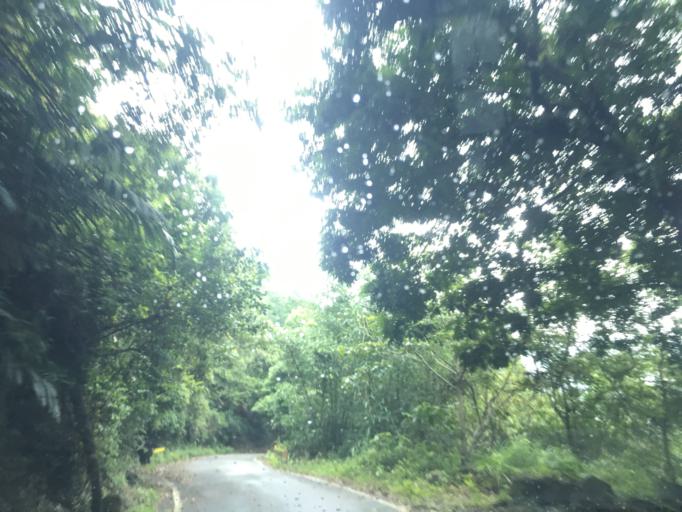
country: TW
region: Taiwan
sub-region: Yunlin
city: Douliu
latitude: 23.5695
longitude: 120.6362
